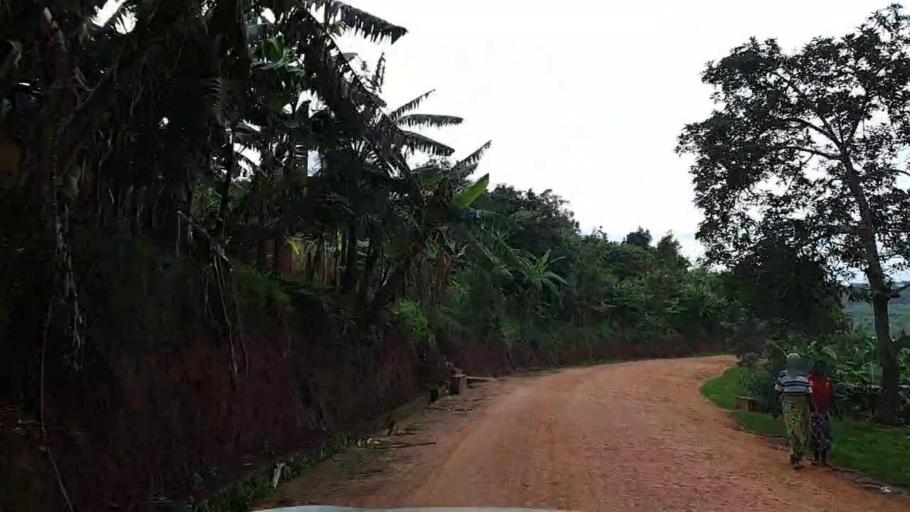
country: RW
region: Southern Province
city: Nyanza
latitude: -2.4157
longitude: 29.6686
